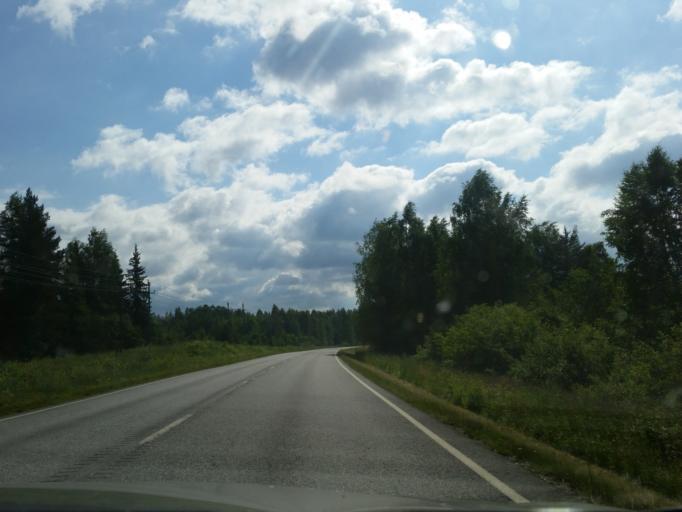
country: FI
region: Northern Savo
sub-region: Kuopio
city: Karttula
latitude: 62.9041
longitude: 26.9677
